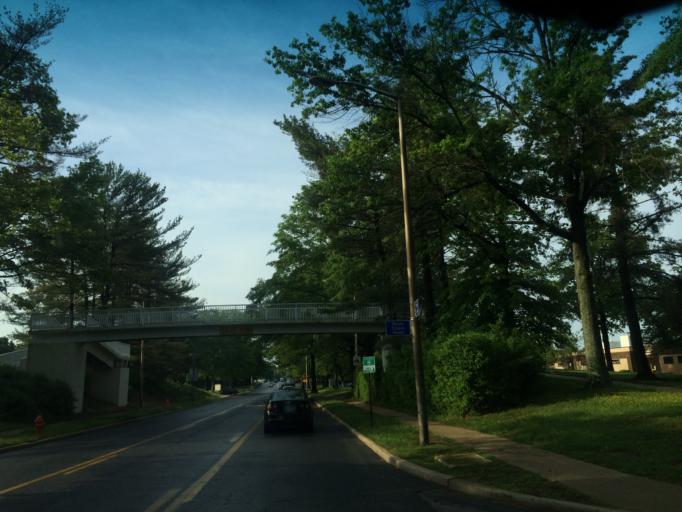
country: US
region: Maryland
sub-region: Howard County
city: Riverside
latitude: 39.2179
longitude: -76.8880
